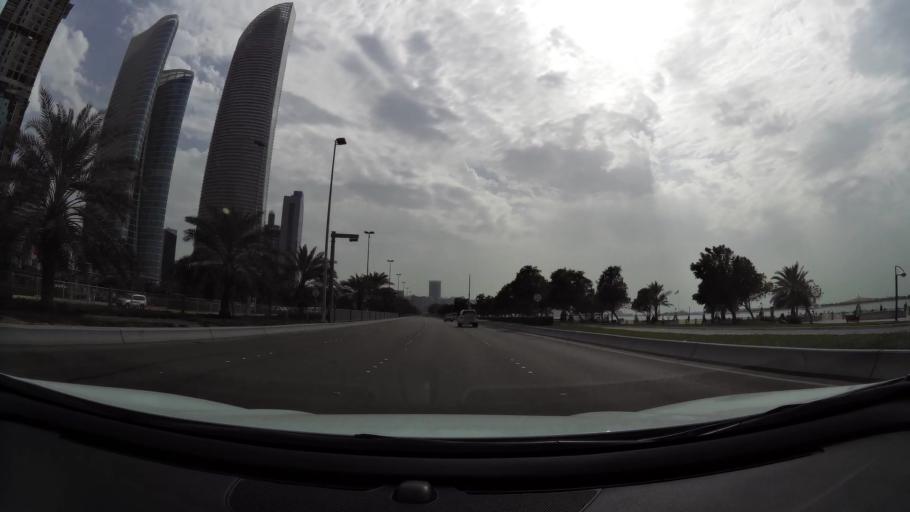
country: AE
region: Abu Dhabi
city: Abu Dhabi
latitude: 24.4887
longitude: 54.3506
